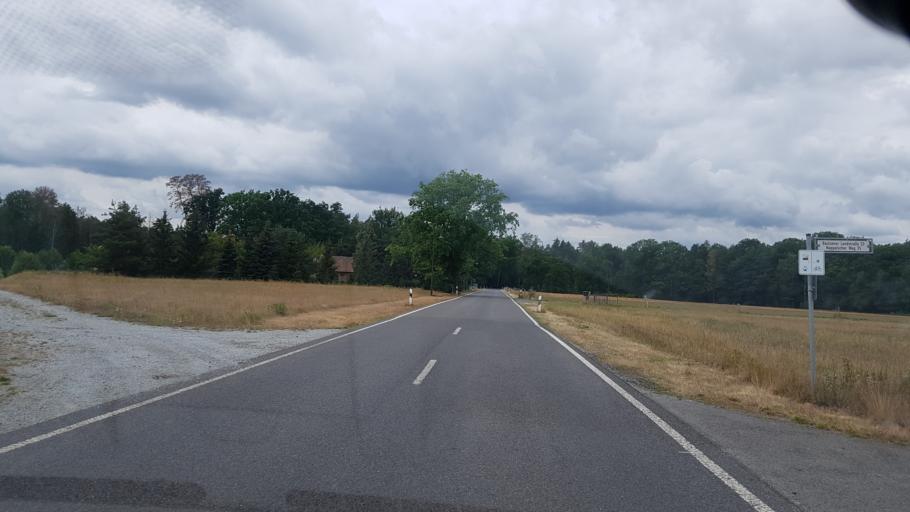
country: DE
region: Saxony
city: Mucka
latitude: 51.3776
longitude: 14.7134
